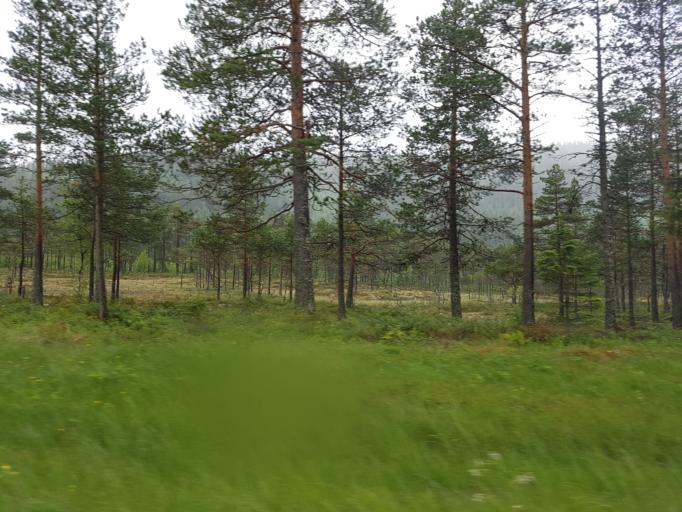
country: NO
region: Nord-Trondelag
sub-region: Stjordal
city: Stjordalshalsen
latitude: 63.3946
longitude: 11.0372
